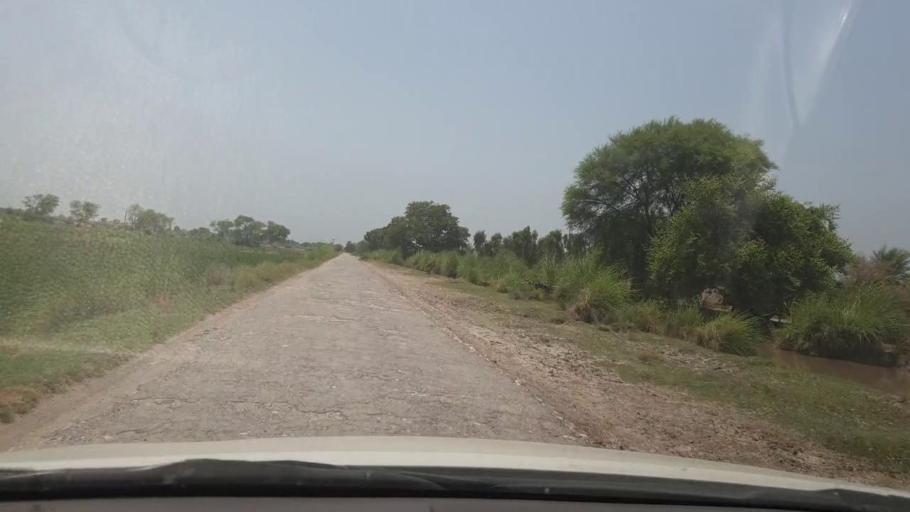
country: PK
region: Sindh
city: Shikarpur
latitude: 28.0896
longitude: 68.5680
